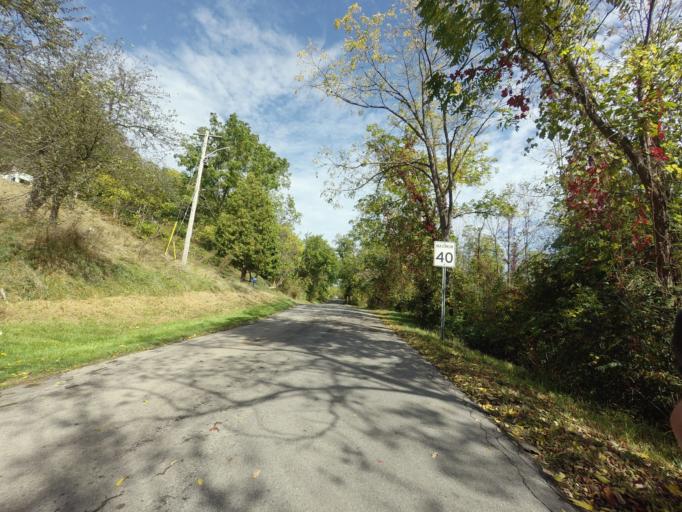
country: CA
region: Ontario
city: Hamilton
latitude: 43.3001
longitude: -79.9220
